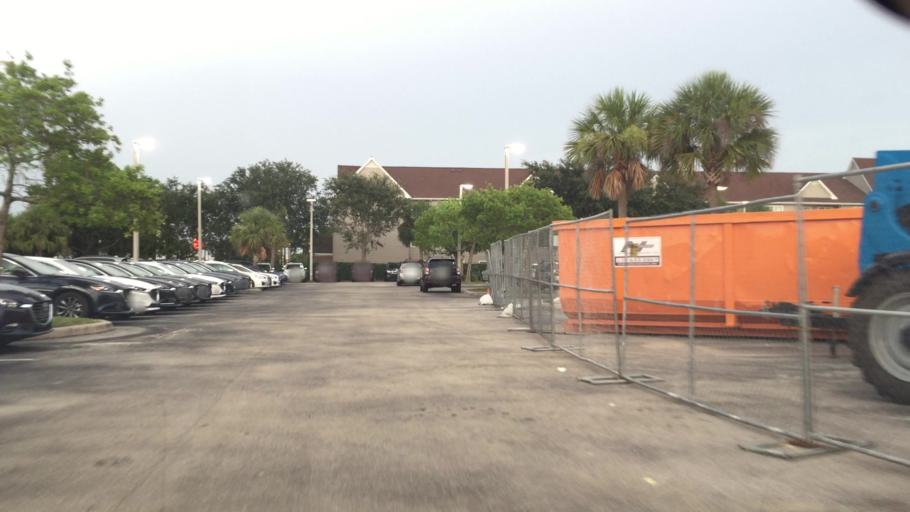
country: US
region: Florida
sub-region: Lee County
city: Fort Myers
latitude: 26.5966
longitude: -81.8528
